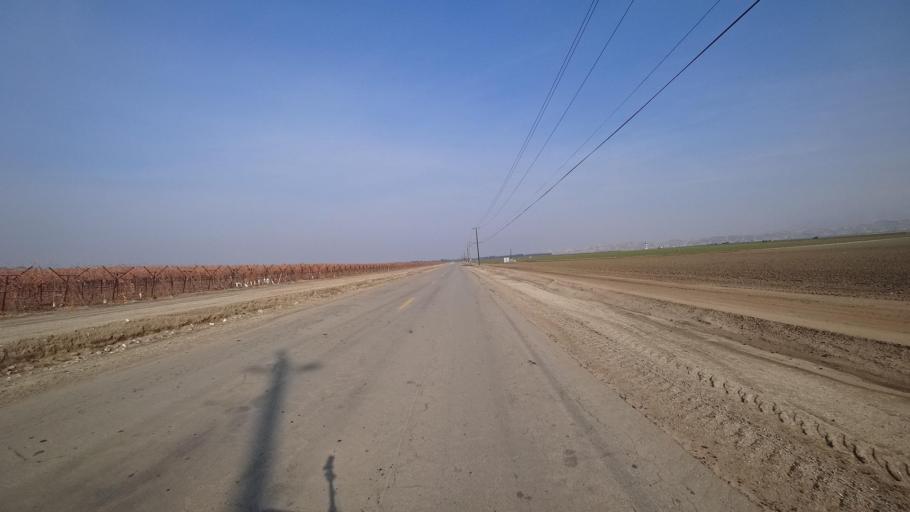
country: US
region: California
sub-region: Kern County
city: Arvin
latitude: 35.0839
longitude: -118.8465
